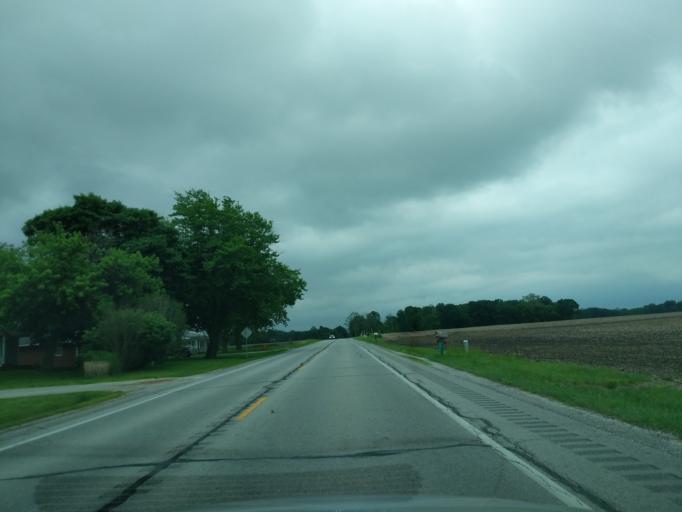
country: US
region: Indiana
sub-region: Madison County
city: Alexandria
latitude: 40.2775
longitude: -85.7057
